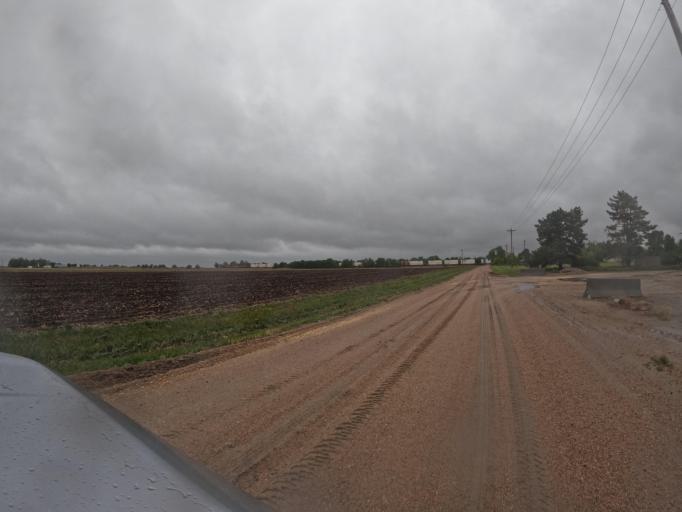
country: US
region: Nebraska
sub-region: Clay County
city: Harvard
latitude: 40.6137
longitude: -98.1027
